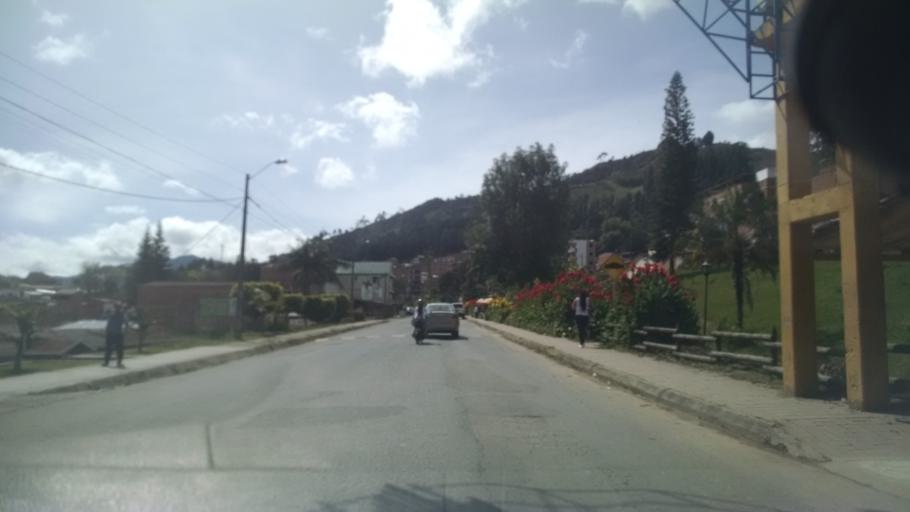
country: CO
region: Antioquia
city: Guatape
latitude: 6.2207
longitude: -75.2460
